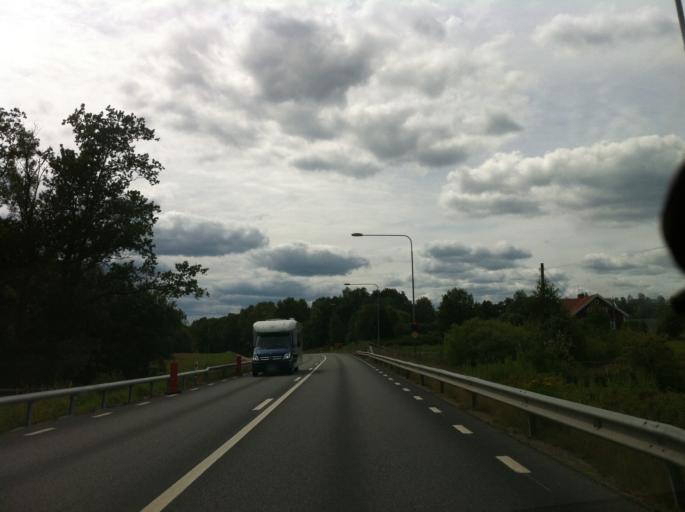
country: SE
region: Kronoberg
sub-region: Tingsryds Kommun
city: Tingsryd
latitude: 56.5293
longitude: 14.9537
